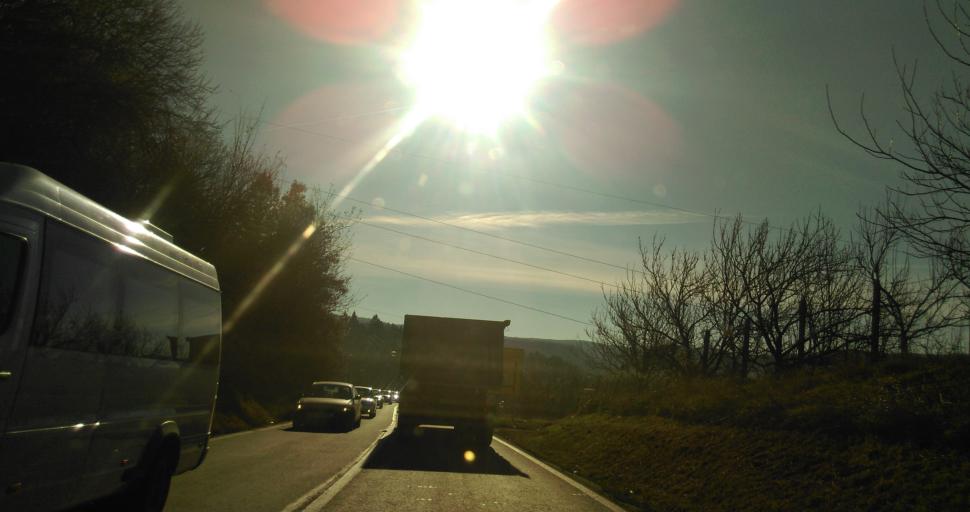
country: RS
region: Autonomna Pokrajina Vojvodina
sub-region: Juznobacki Okrug
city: Novi Sad
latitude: 45.2088
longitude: 19.8442
